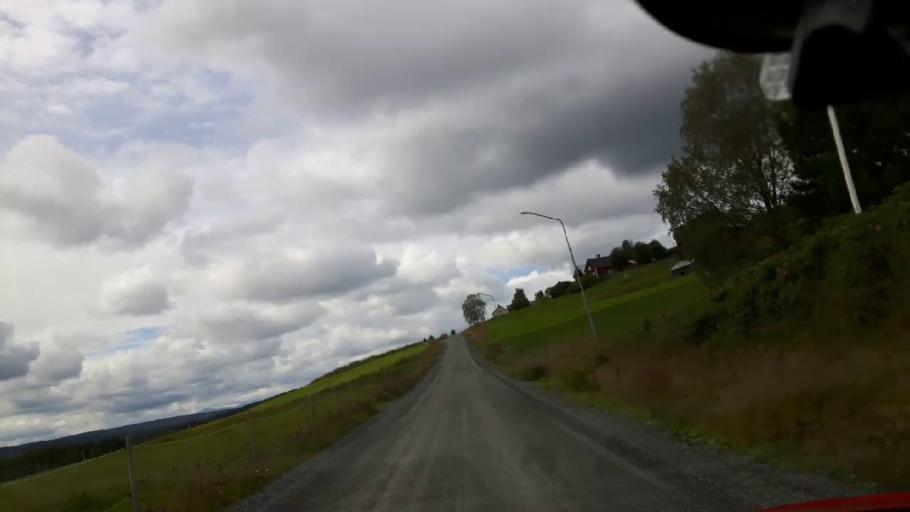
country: SE
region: Jaemtland
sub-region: Krokoms Kommun
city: Valla
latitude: 63.4876
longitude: 13.9981
